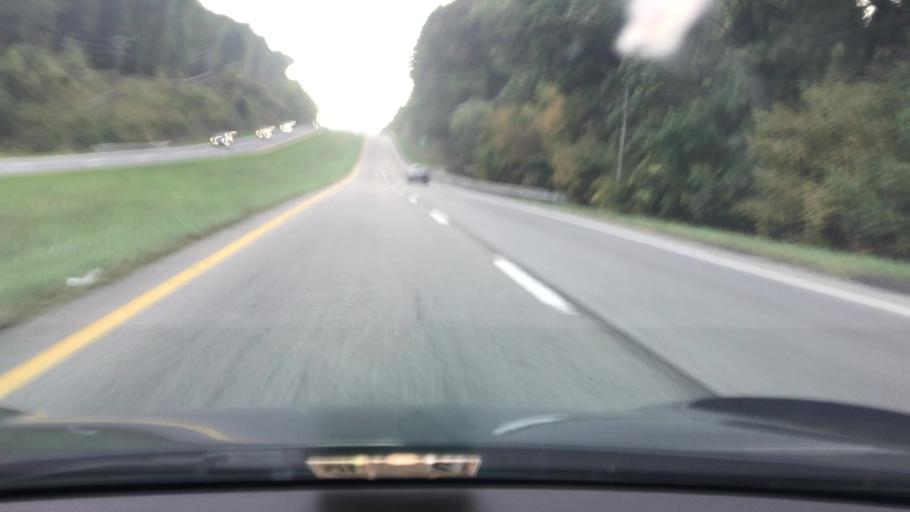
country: US
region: Virginia
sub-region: Botetourt County
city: Blue Ridge
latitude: 37.3962
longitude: -79.7700
